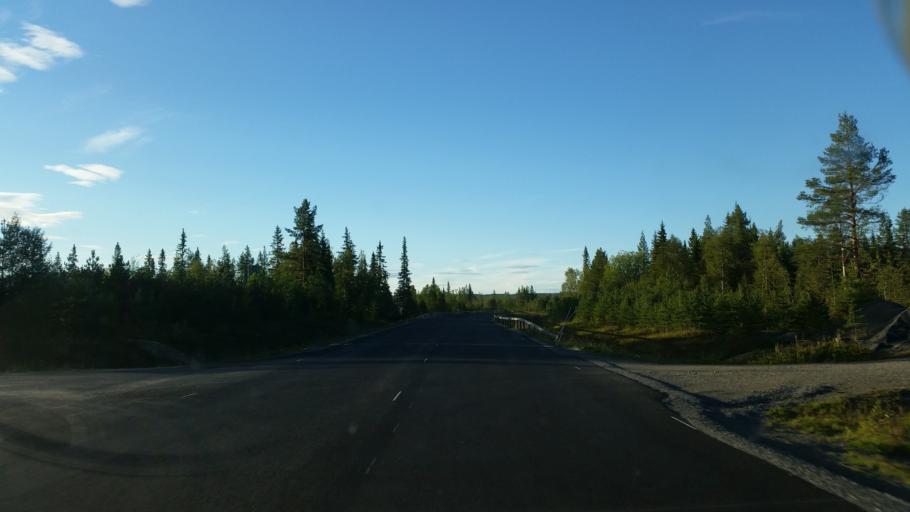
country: SE
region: Vaesterbotten
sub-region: Dorotea Kommun
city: Dorotea
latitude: 64.3372
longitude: 16.6413
